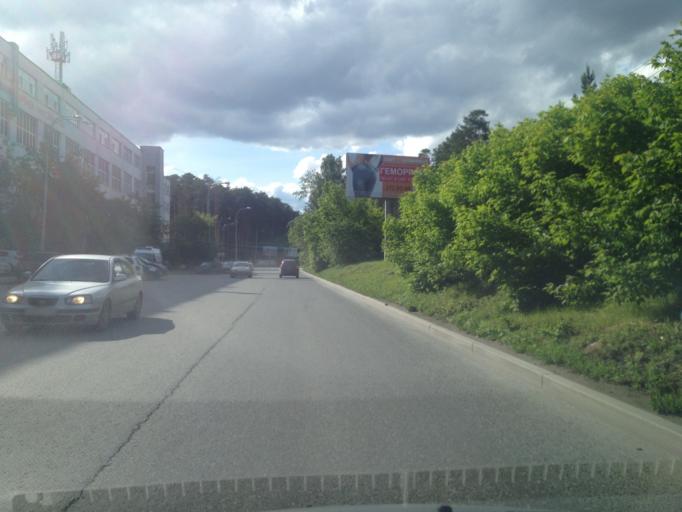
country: RU
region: Sverdlovsk
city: Sovkhoznyy
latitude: 56.8134
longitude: 60.5377
